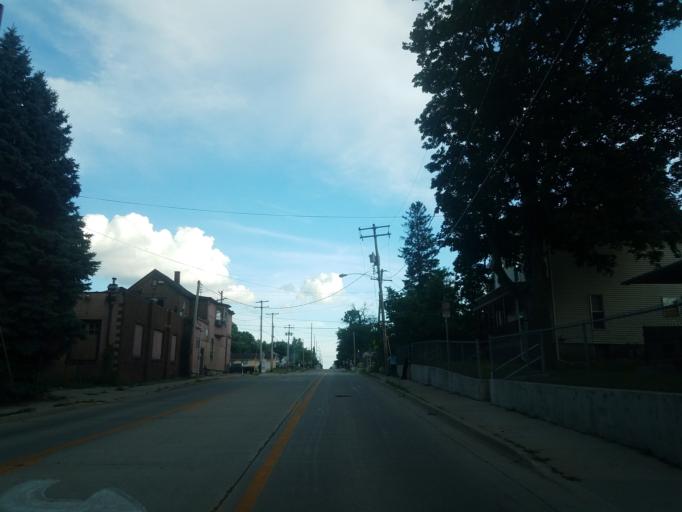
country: US
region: Illinois
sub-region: McLean County
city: Bloomington
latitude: 40.4756
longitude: -89.0065
